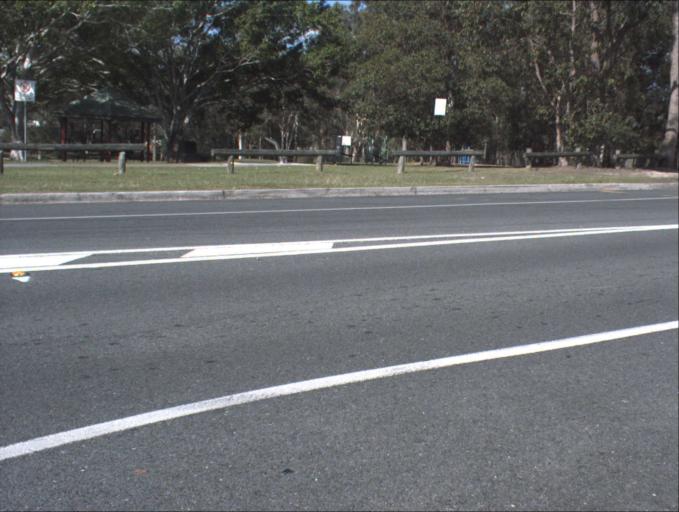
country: AU
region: Queensland
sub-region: Logan
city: Park Ridge South
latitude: -27.6914
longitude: 153.0175
